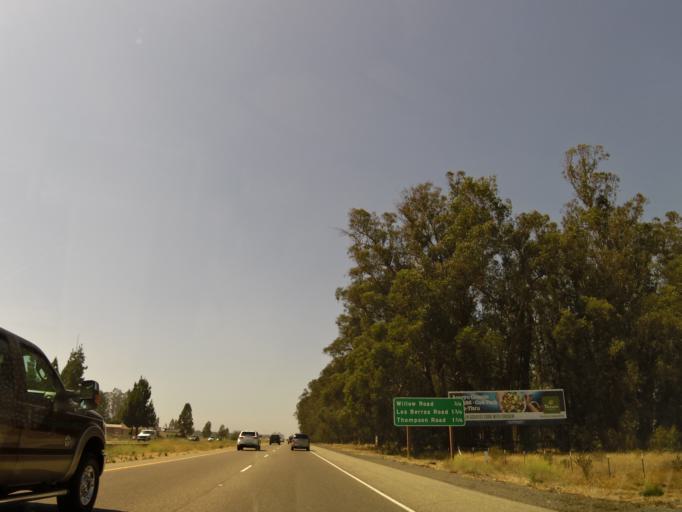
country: US
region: California
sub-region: San Luis Obispo County
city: Nipomo
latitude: 35.0434
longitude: -120.4904
